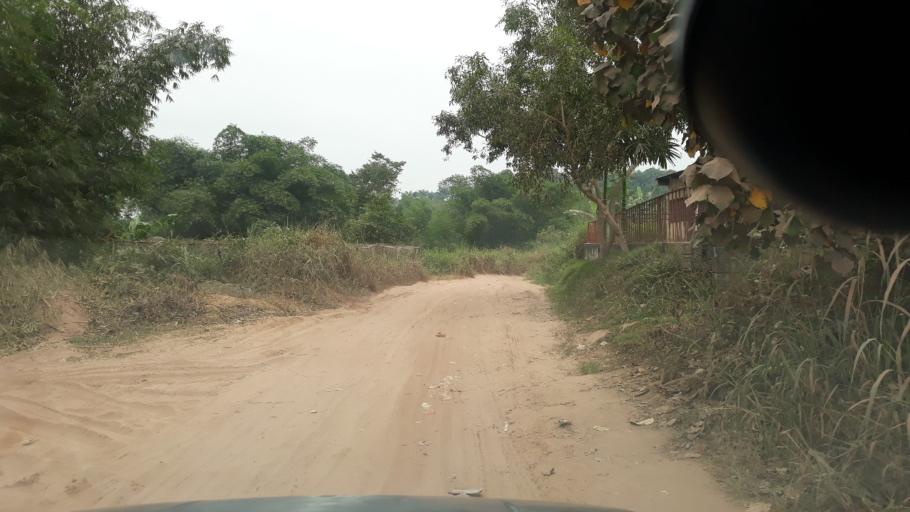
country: CD
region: Kinshasa
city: Masina
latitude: -4.4782
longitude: 15.2742
